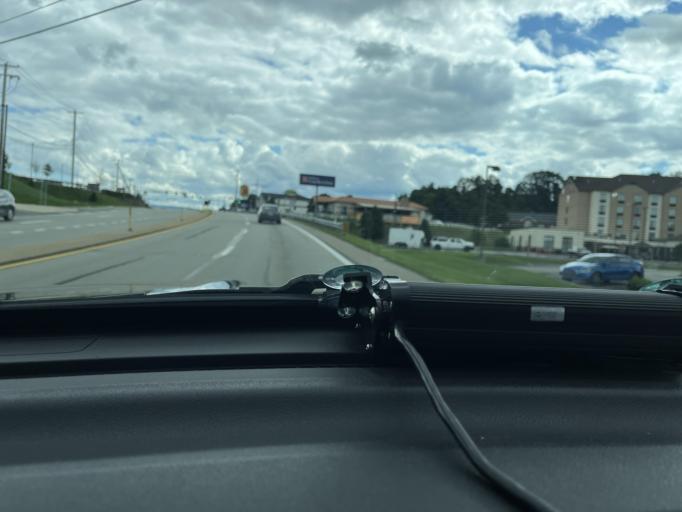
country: US
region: Pennsylvania
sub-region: Fayette County
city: South Uniontown
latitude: 39.9151
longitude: -79.7512
